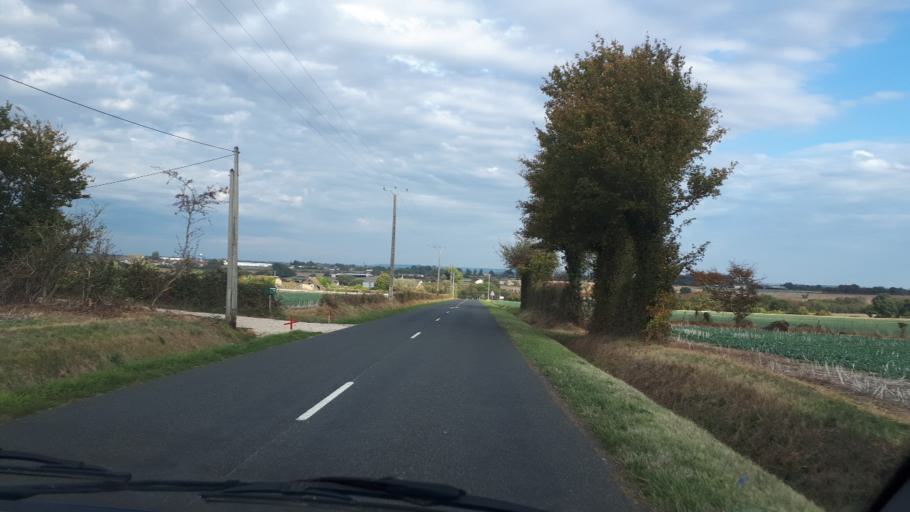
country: FR
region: Centre
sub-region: Departement du Loir-et-Cher
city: Mondoubleau
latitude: 47.9687
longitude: 0.9245
